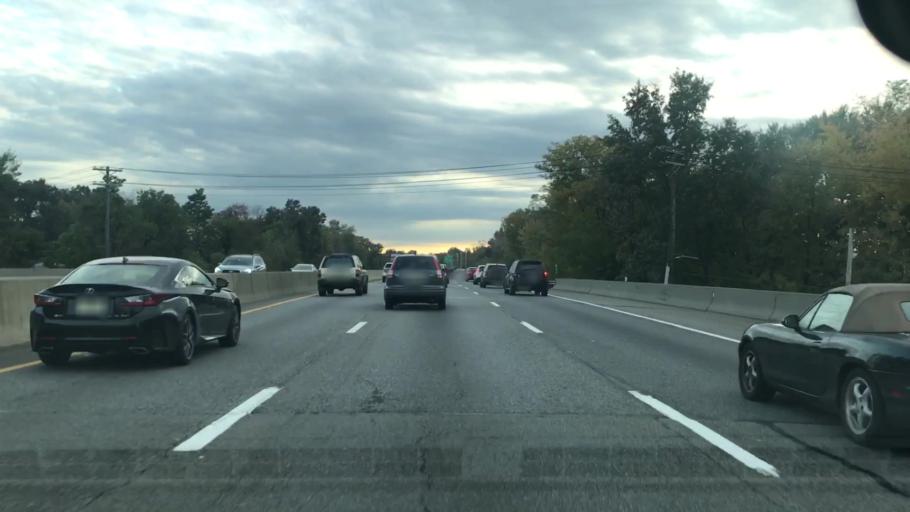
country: US
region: New Jersey
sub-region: Bergen County
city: Elmwood Park
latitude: 40.8987
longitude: -74.1149
